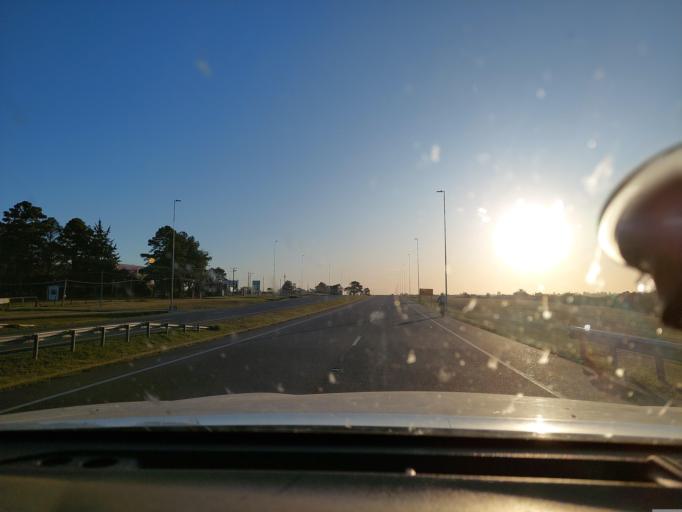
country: UY
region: Canelones
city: Pando
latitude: -34.7056
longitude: -55.9265
